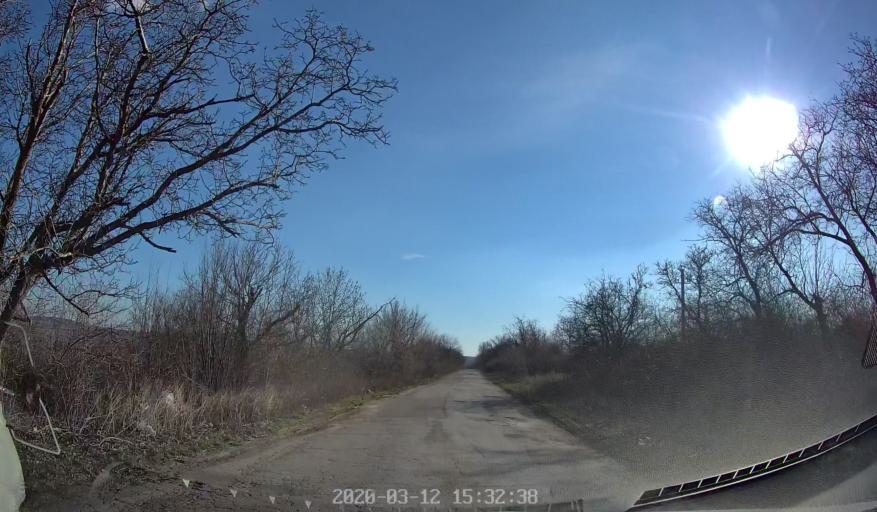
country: MD
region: Chisinau
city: Ciorescu
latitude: 47.1501
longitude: 28.9403
